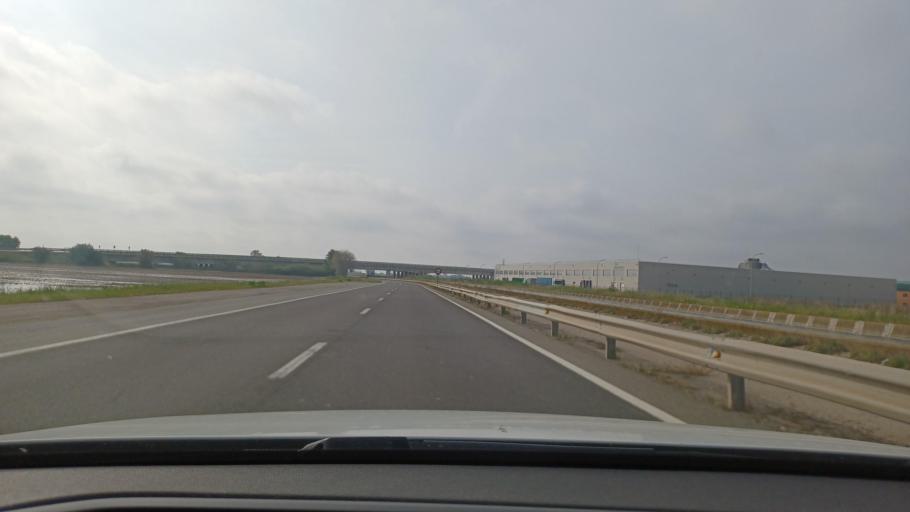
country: ES
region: Catalonia
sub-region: Provincia de Tarragona
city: Amposta
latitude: 40.7163
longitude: 0.5899
